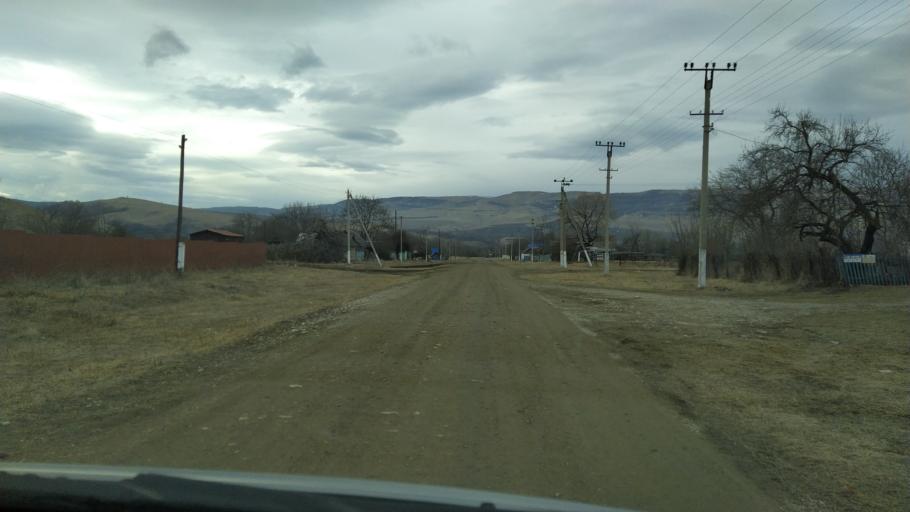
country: RU
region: Krasnodarskiy
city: Peredovaya
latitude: 44.0824
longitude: 41.3687
